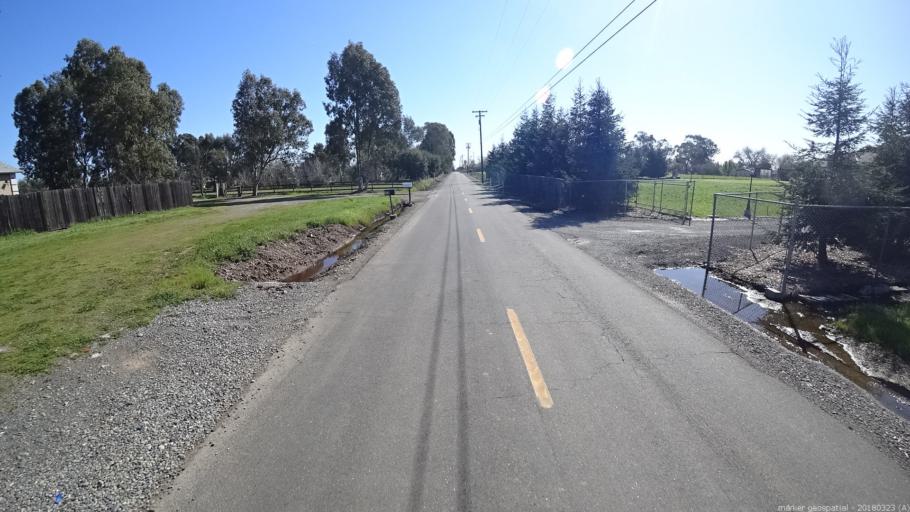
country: US
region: California
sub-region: Sacramento County
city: Elverta
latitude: 38.7052
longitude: -121.4725
